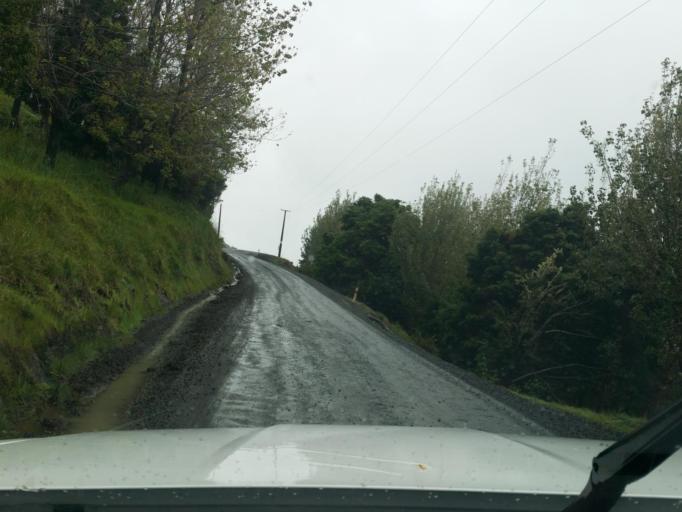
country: NZ
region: Northland
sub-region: Kaipara District
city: Dargaville
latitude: -35.7727
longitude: 173.9888
